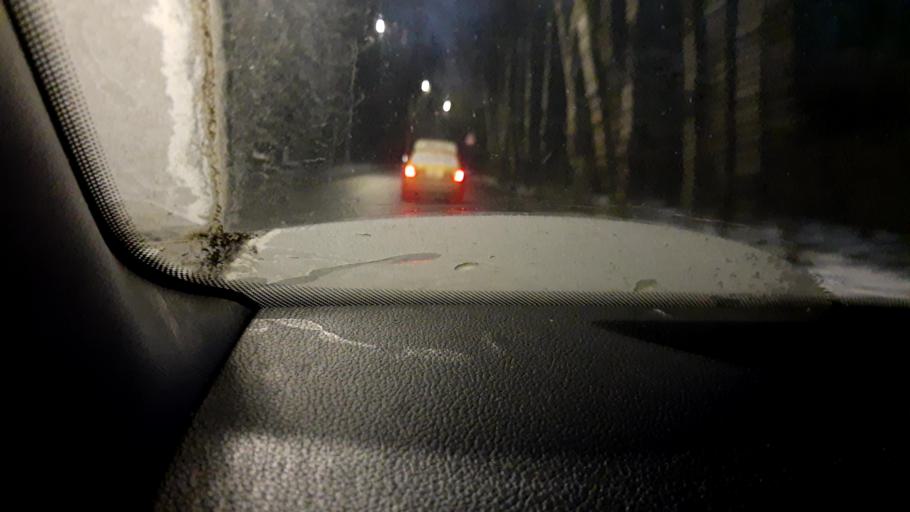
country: RU
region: Moscow
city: Annino
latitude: 55.5505
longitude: 37.6235
